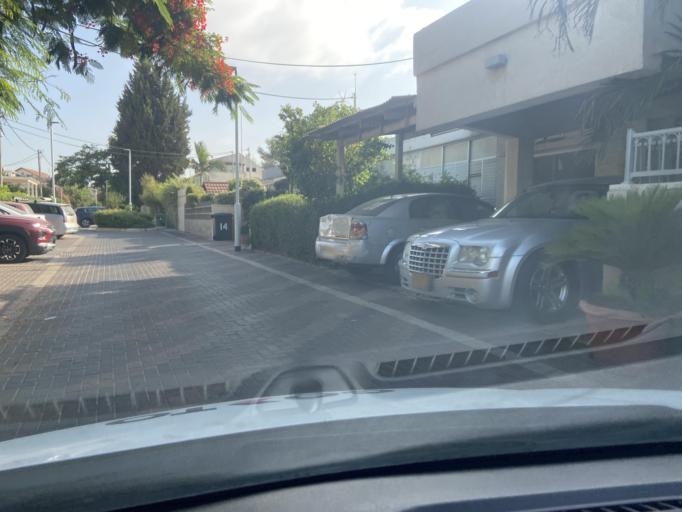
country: IL
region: Central District
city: Yehud
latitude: 32.0306
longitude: 34.8816
